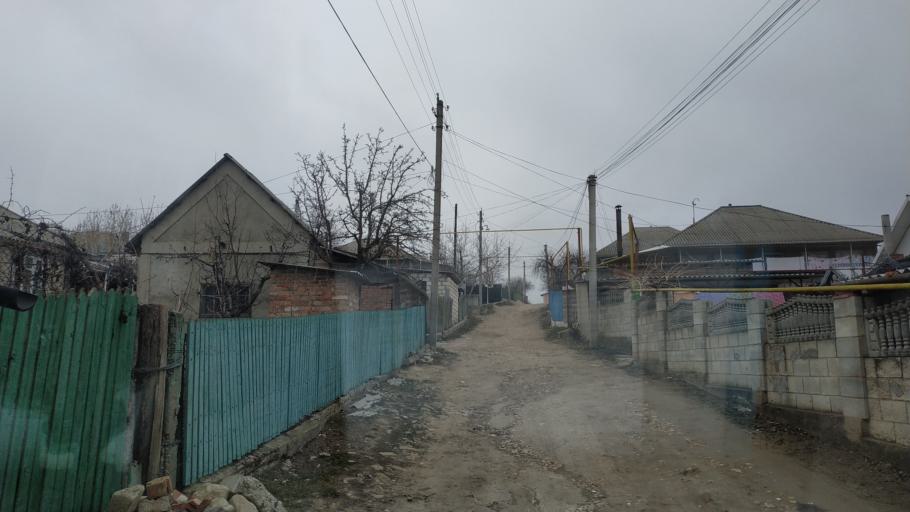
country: MD
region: Hincesti
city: Hincesti
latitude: 46.9083
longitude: 28.6657
